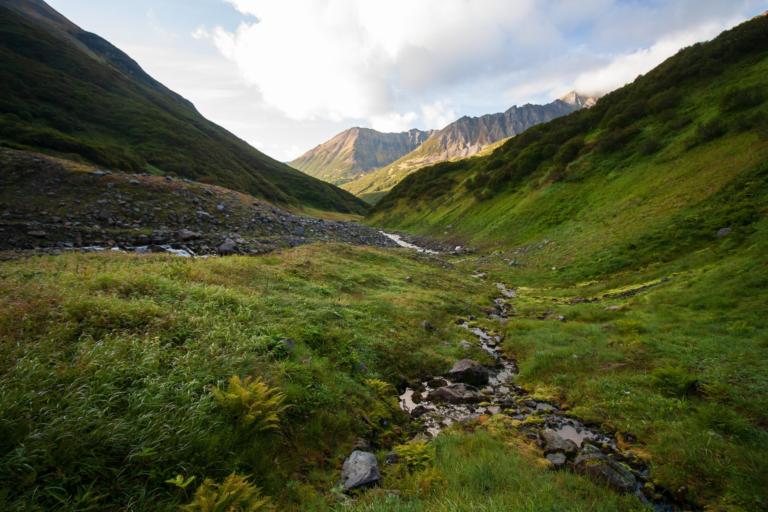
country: RU
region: Kamtsjatka
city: Yelizovo
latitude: 53.8578
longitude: 158.2655
